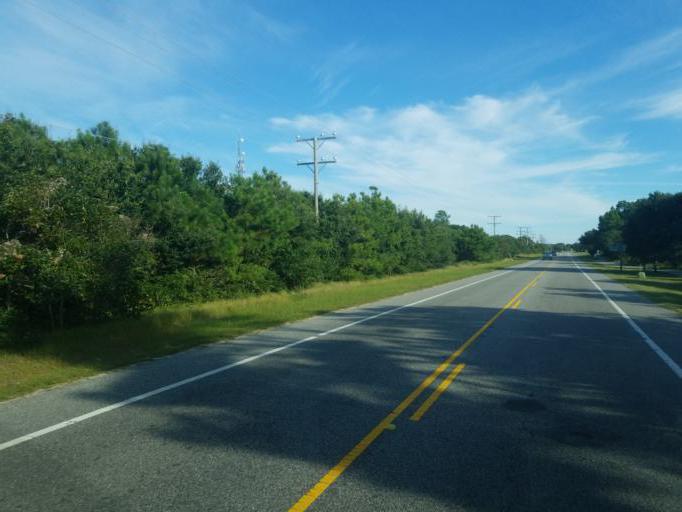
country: US
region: North Carolina
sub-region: Dare County
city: Southern Shores
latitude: 36.3195
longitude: -75.8150
